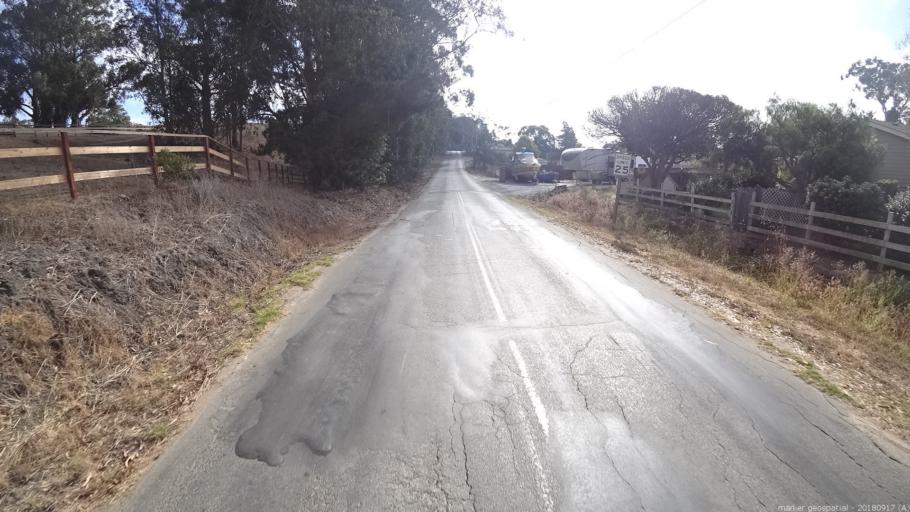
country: US
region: California
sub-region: Monterey County
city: Elkhorn
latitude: 36.7897
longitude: -121.7230
